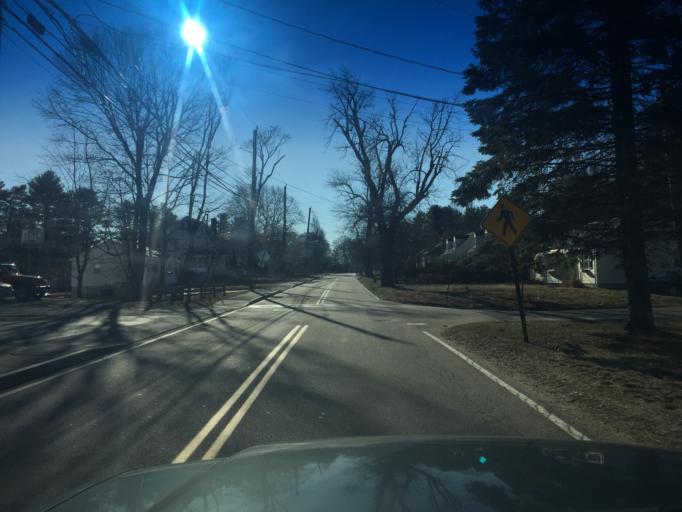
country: US
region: Massachusetts
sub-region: Norfolk County
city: Millis
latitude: 42.1783
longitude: -71.3612
